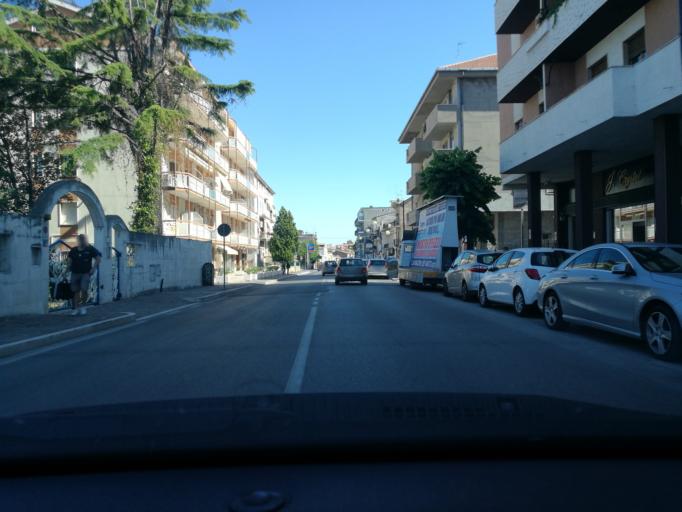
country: IT
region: Abruzzo
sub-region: Provincia di Chieti
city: Vasto
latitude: 42.1192
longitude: 14.7077
